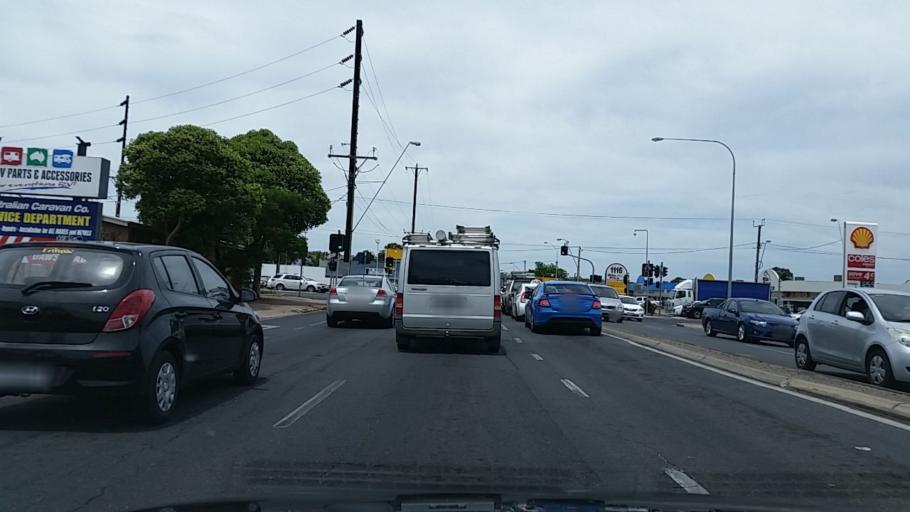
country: AU
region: South Australia
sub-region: Marion
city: Clovelly Park
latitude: -34.9921
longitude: 138.5749
